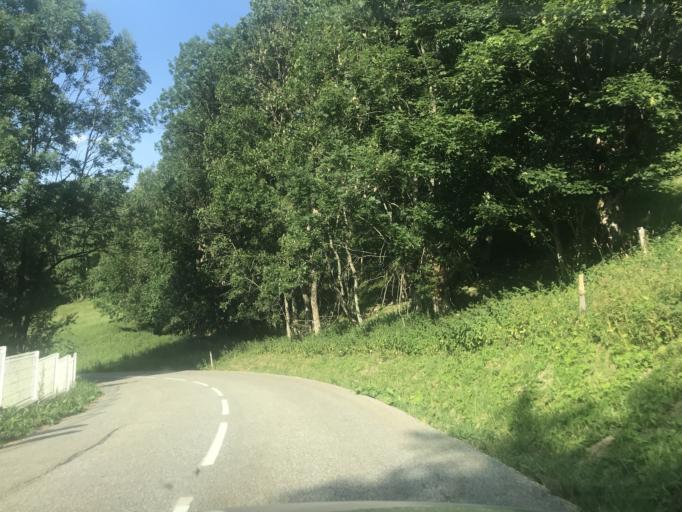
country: FR
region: Rhone-Alpes
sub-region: Departement de la Savoie
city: Saint-Etienne-de-Cuines
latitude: 45.2809
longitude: 6.2129
